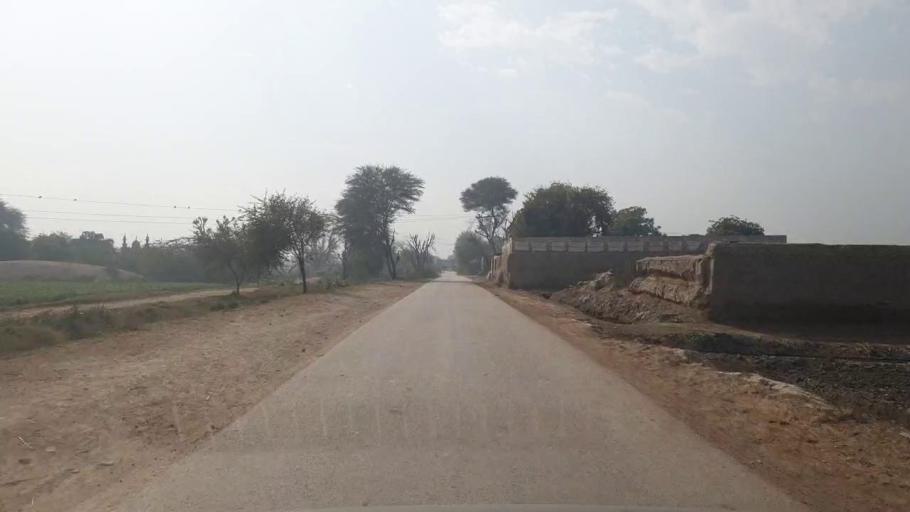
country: PK
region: Sindh
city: Hala
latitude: 25.7531
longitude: 68.4455
